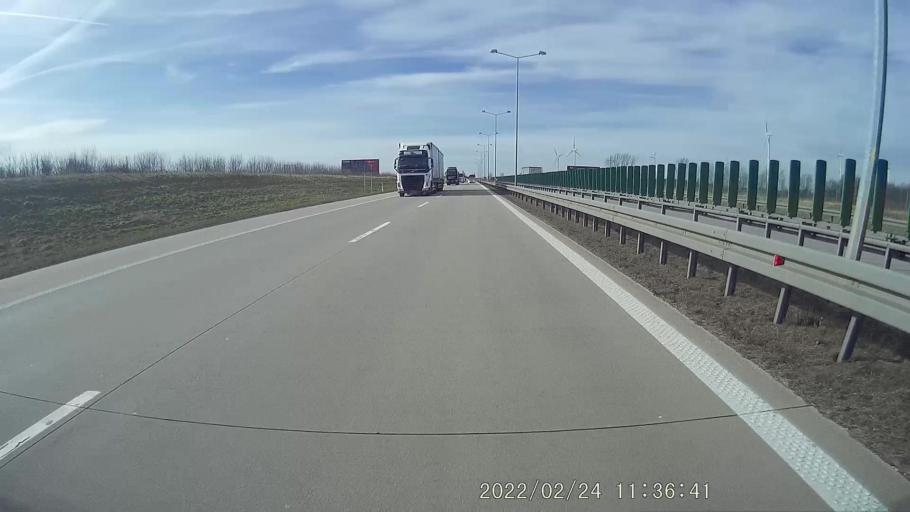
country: PL
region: Lower Silesian Voivodeship
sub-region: Powiat polkowicki
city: Przemkow
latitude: 51.5218
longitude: 15.8108
